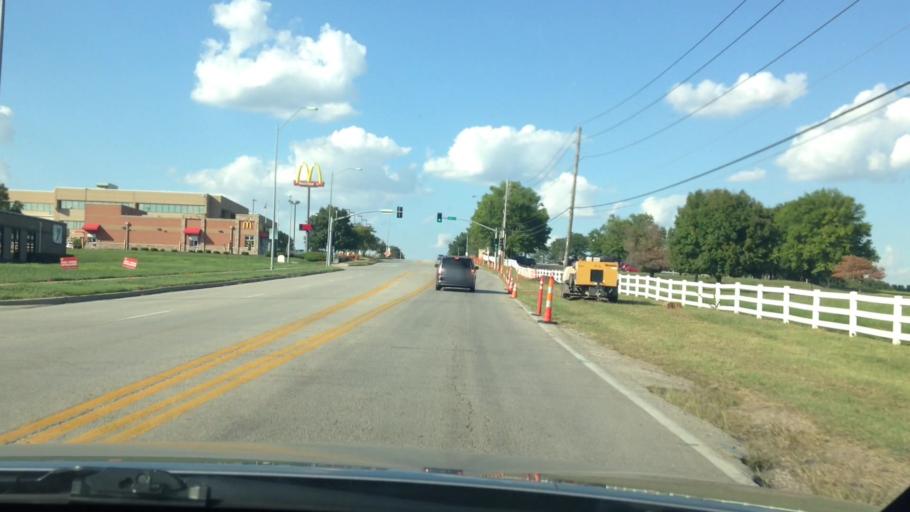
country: US
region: Kansas
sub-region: Johnson County
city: Leawood
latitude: 38.9202
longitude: -94.5838
